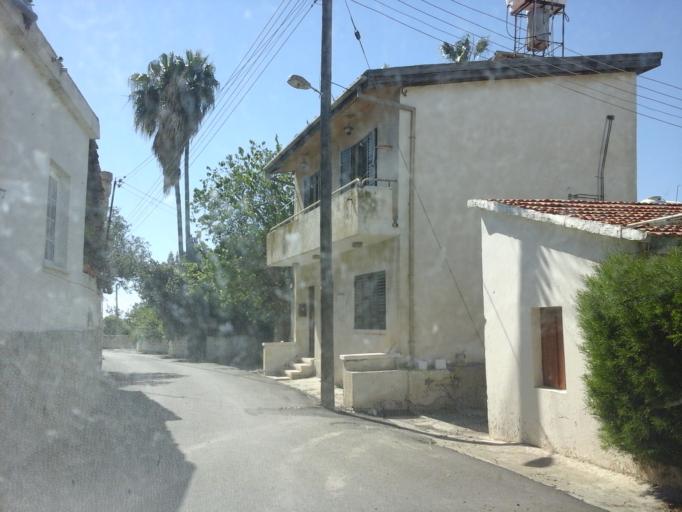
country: CY
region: Larnaka
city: Kolossi
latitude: 34.6683
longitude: 32.9324
